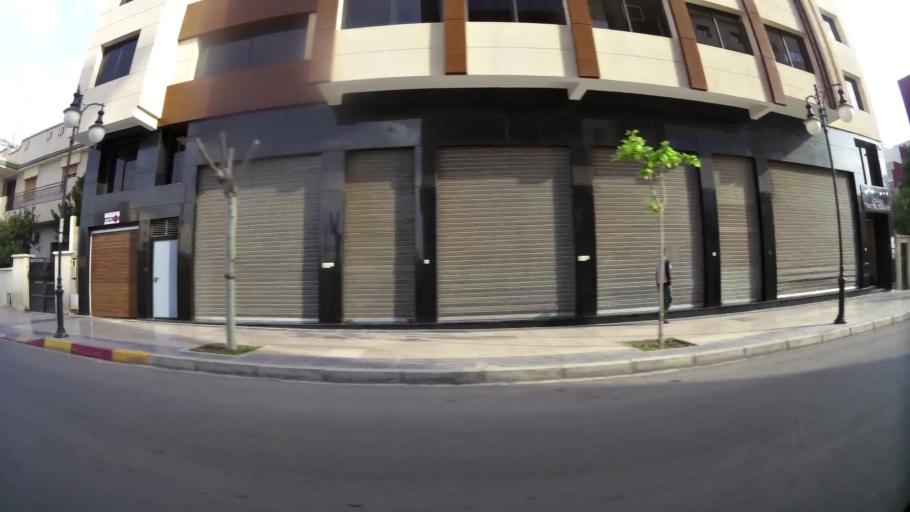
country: MA
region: Oriental
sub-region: Oujda-Angad
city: Oujda
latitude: 34.6780
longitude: -1.9213
